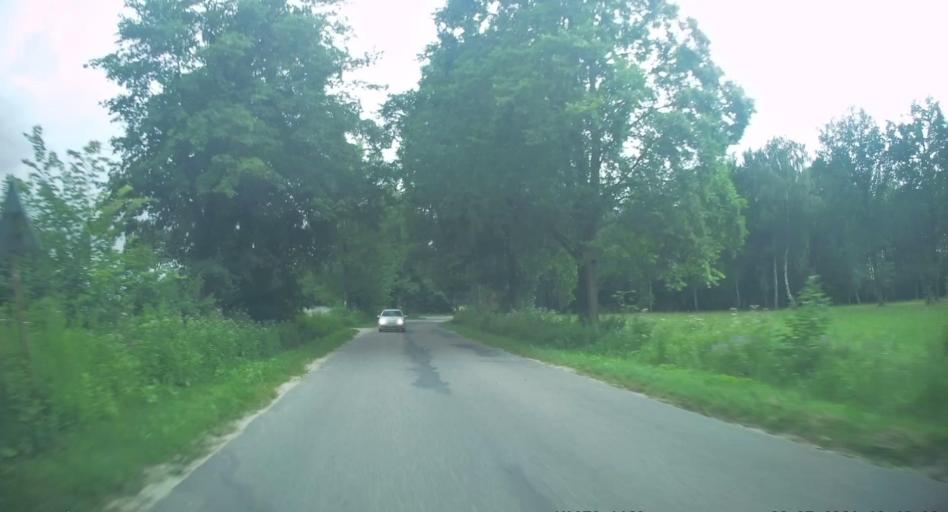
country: PL
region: Lodz Voivodeship
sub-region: Powiat rawski
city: Rawa Mazowiecka
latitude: 51.7457
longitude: 20.1858
